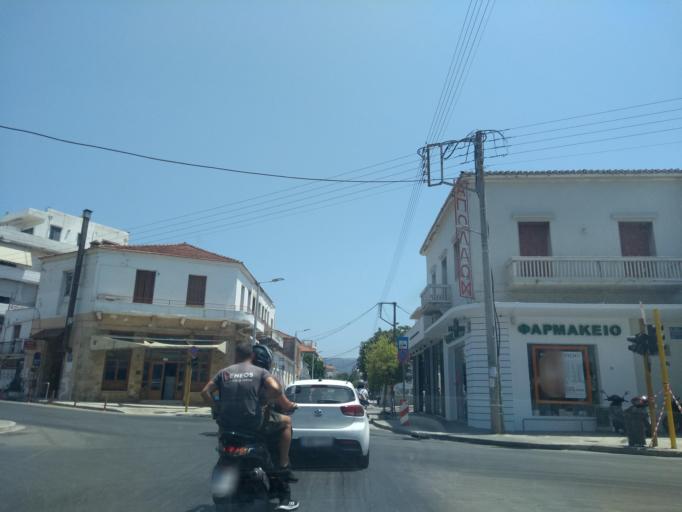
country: GR
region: Crete
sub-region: Nomos Chanias
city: Chania
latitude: 35.5107
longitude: 24.0218
